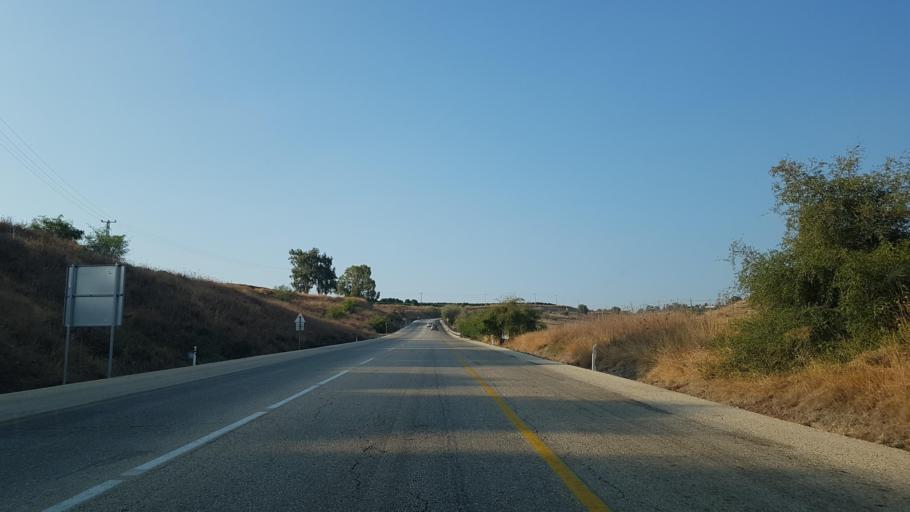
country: SY
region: Quneitra
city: Al Butayhah
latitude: 32.8949
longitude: 35.5977
